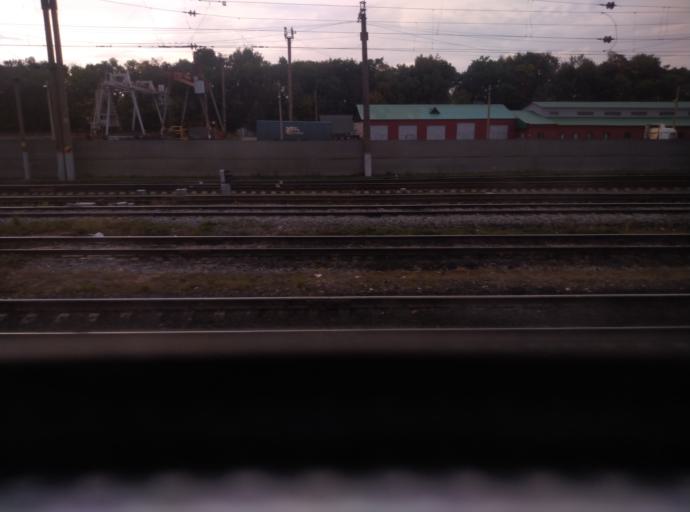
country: RU
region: Jaroslavl
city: Yaroslavl
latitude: 57.5984
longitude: 39.8617
